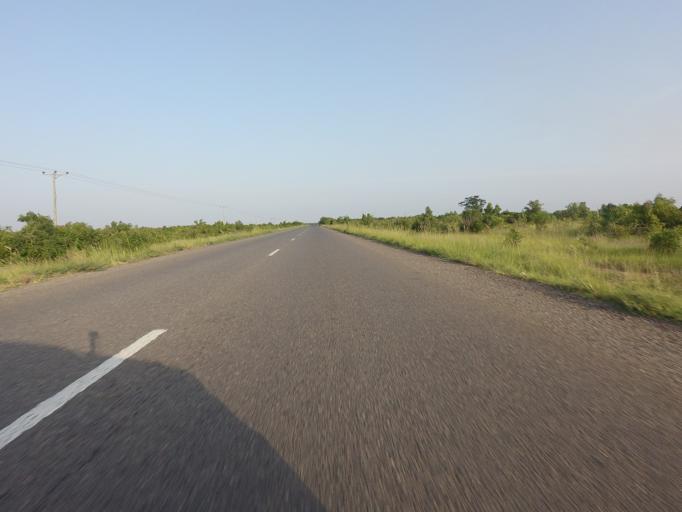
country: GH
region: Volta
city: Anloga
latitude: 5.9625
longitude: 0.6647
